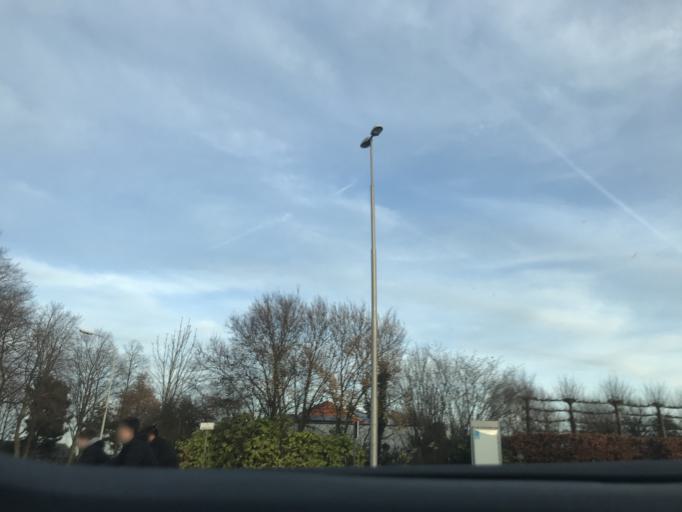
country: BE
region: Flanders
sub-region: Provincie Oost-Vlaanderen
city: Destelbergen
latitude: 51.1015
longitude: 3.7818
